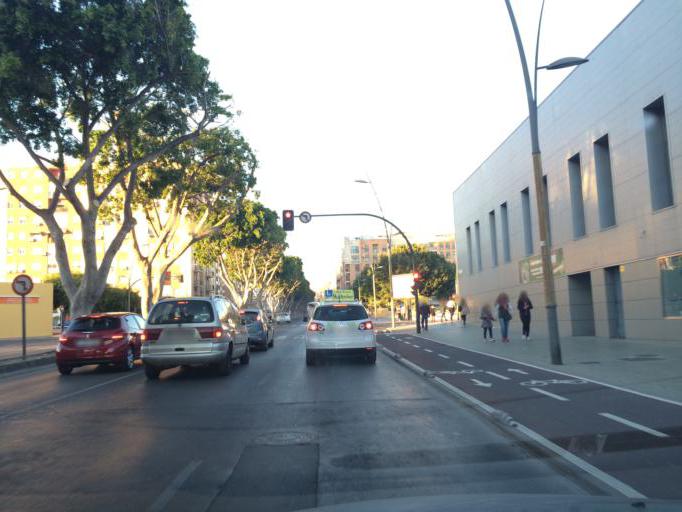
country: ES
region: Andalusia
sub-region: Provincia de Almeria
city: Almeria
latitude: 36.8406
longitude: -2.4473
